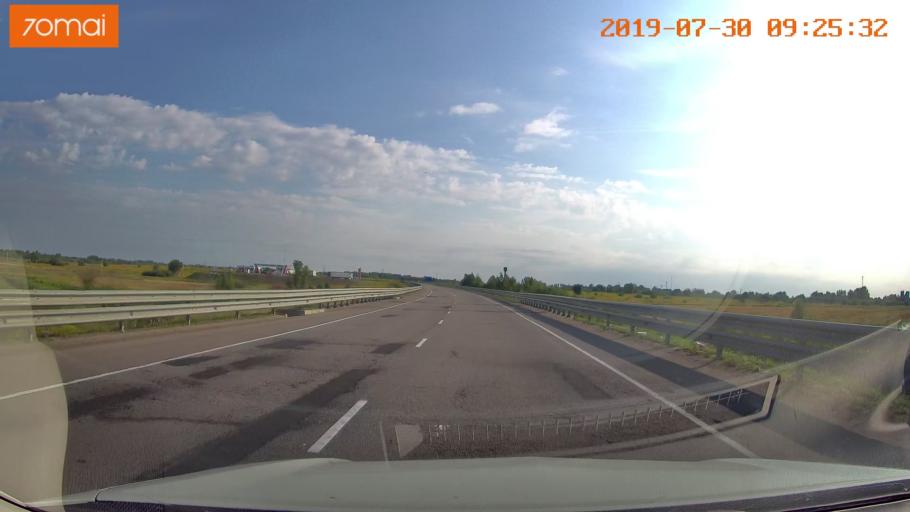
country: LT
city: Kybartai
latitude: 54.6403
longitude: 22.7180
